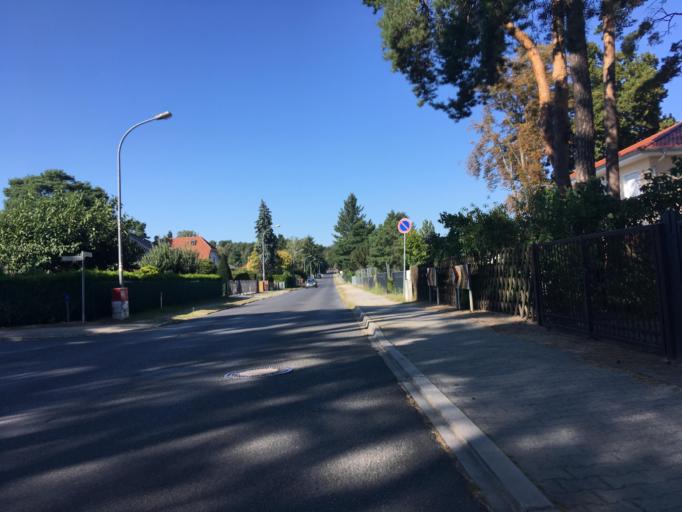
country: DE
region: Brandenburg
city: Wildau
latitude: 52.3278
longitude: 13.6356
